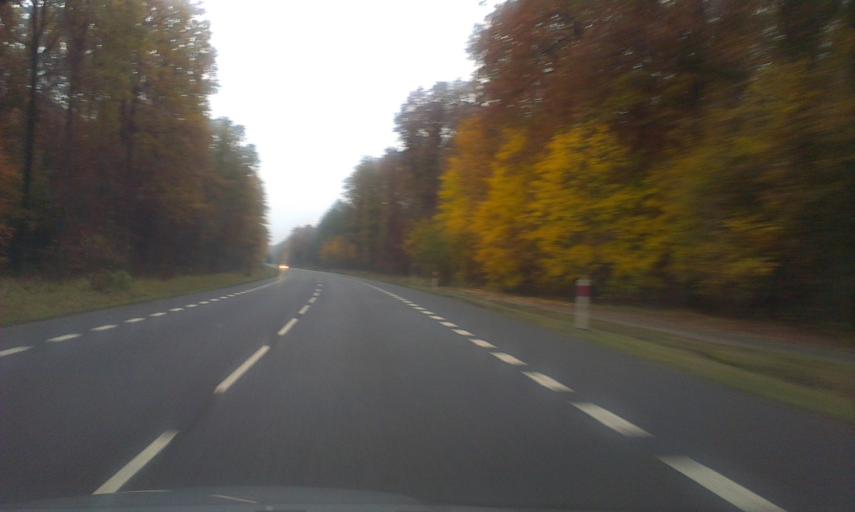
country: PL
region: Greater Poland Voivodeship
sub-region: Powiat chodzieski
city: Budzyn
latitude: 52.9121
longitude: 16.9732
